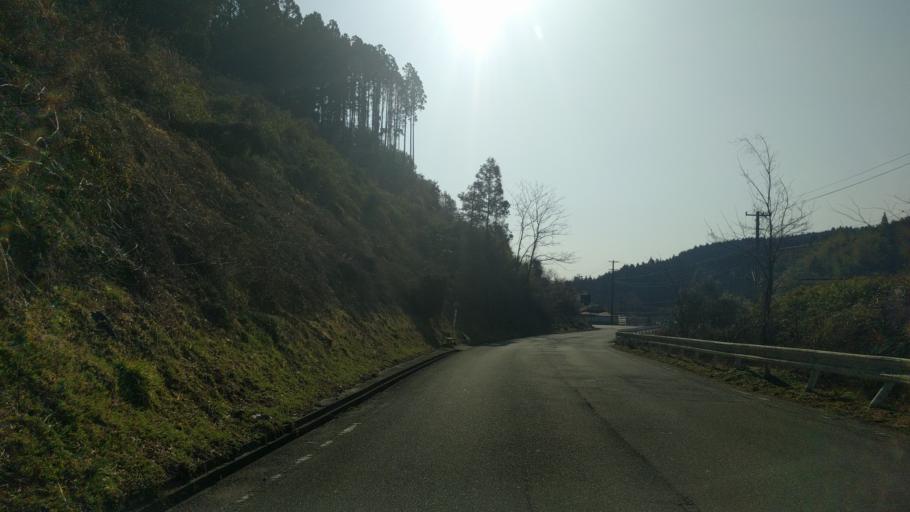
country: JP
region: Fukushima
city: Iwaki
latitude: 37.0173
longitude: 140.8168
